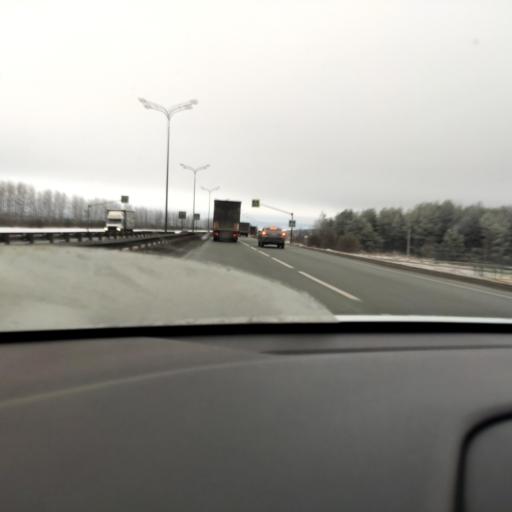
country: RU
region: Tatarstan
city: Osinovo
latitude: 55.7613
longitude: 48.8165
